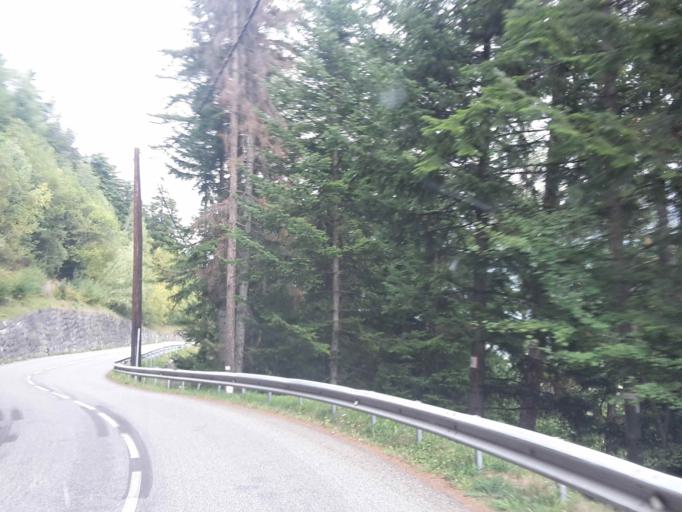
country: FR
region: Rhone-Alpes
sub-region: Departement de la Savoie
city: Saint-Michel-de-Maurienne
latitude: 45.1992
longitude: 6.4683
